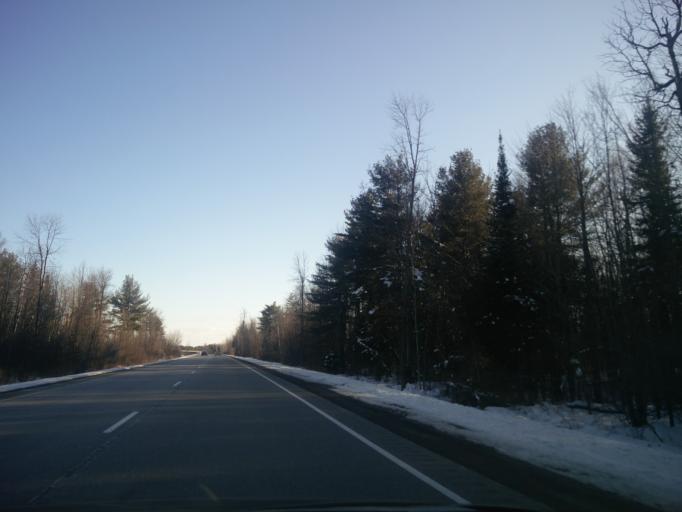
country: CA
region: Ontario
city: Prescott
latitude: 44.9135
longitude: -75.5761
